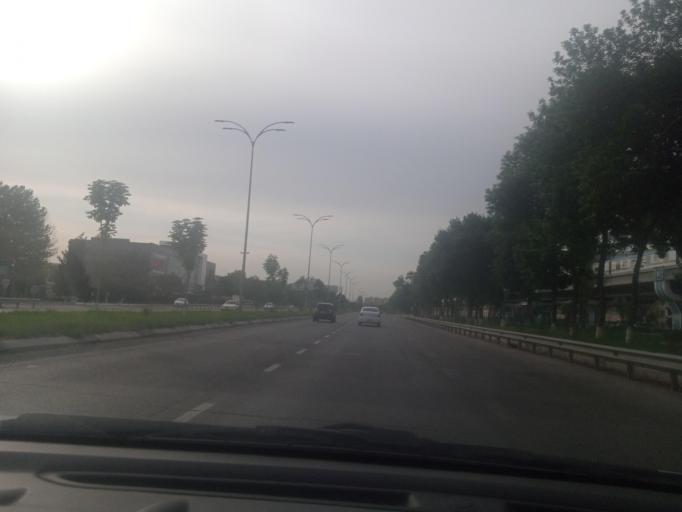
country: UZ
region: Toshkent
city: Salor
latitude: 41.2995
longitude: 69.3474
